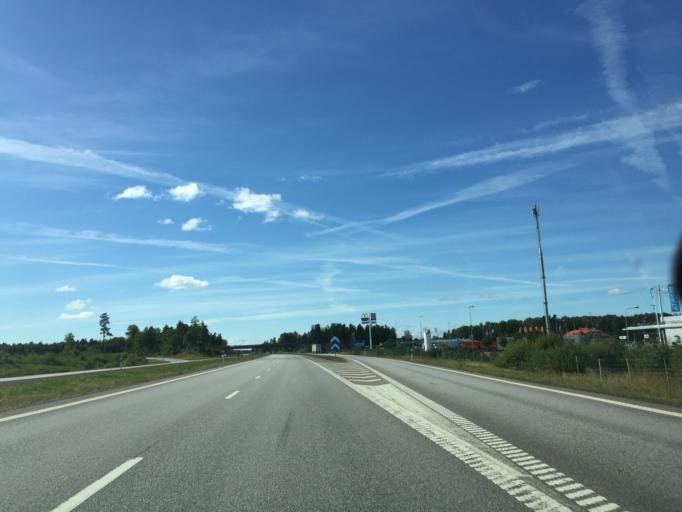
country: SE
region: Vaestmanland
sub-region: Arboga Kommun
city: Arboga
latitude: 59.4255
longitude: 15.8348
